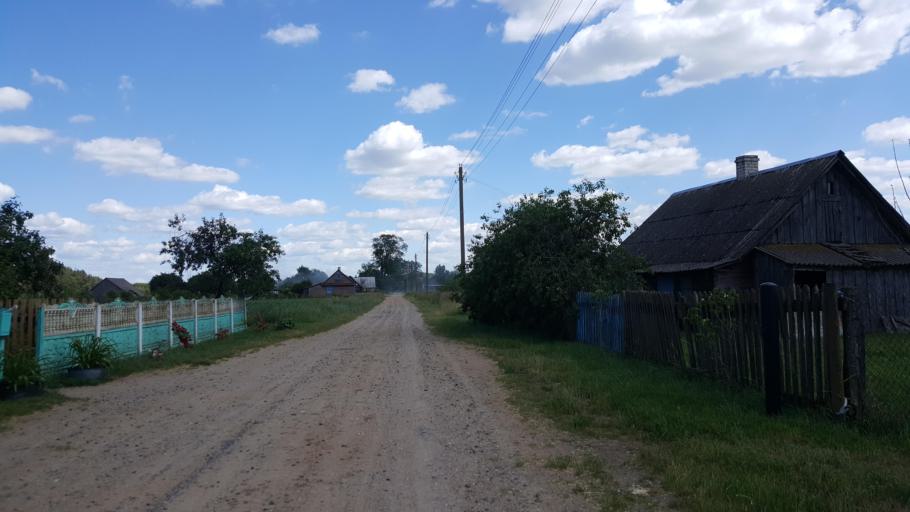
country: BY
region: Brest
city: Kamyanyuki
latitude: 52.5368
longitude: 23.5996
